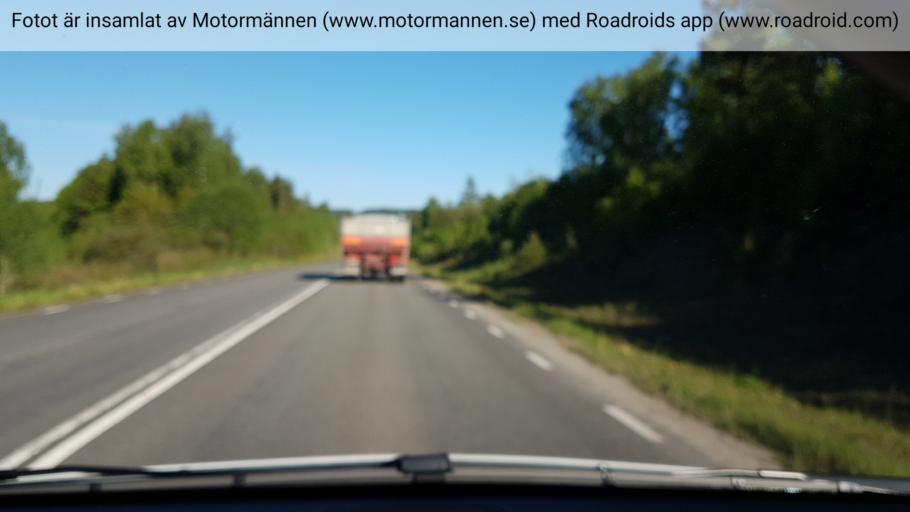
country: SE
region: Vaestra Goetaland
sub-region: Skovde Kommun
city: Stopen
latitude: 58.5318
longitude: 13.7666
